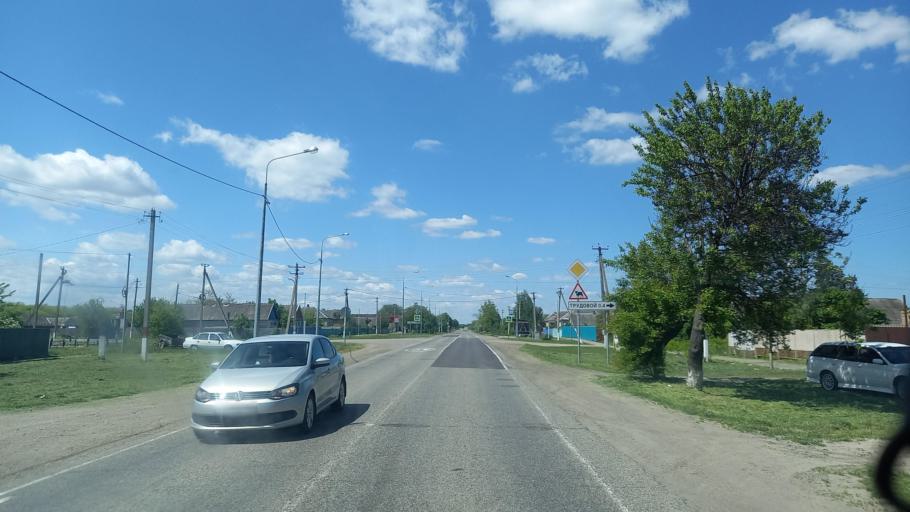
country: RU
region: Krasnodarskiy
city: Tbilisskaya
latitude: 45.3286
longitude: 40.2826
